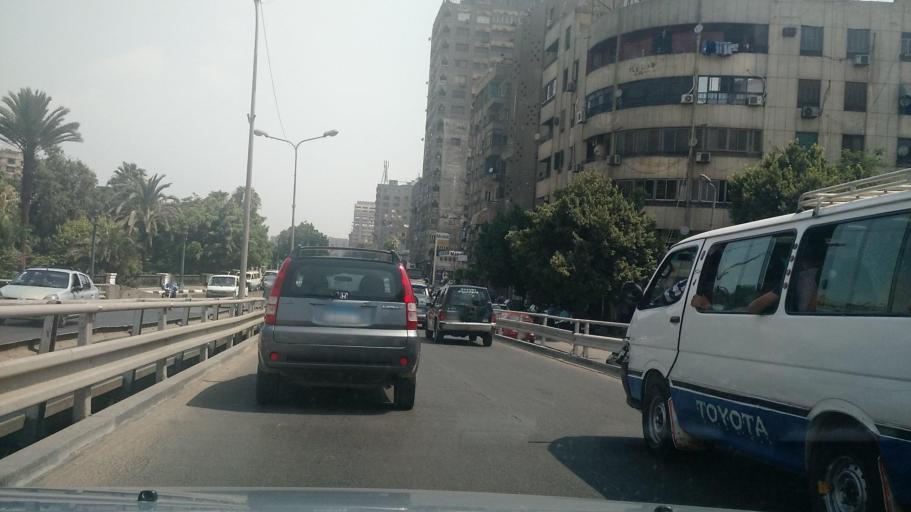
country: EG
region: Al Jizah
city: Al Jizah
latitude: 30.0173
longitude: 31.2291
